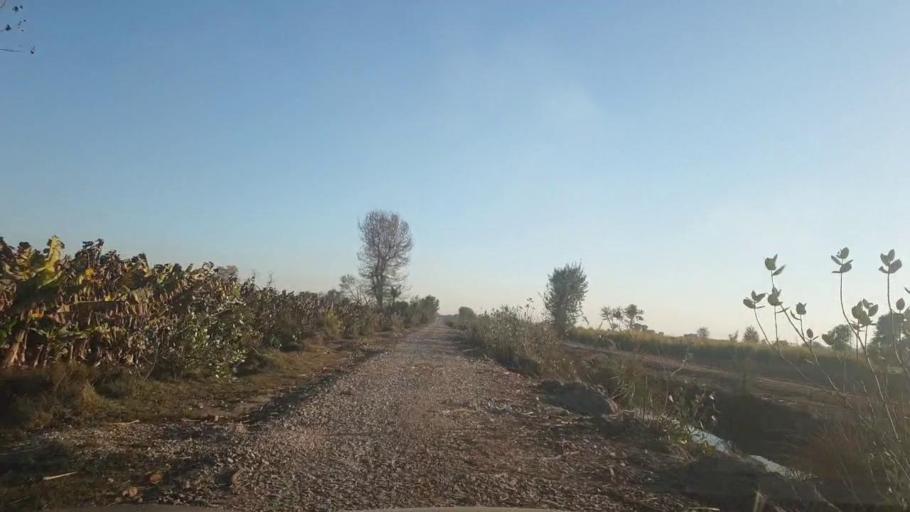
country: PK
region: Sindh
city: Ghotki
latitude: 28.0152
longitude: 69.2679
